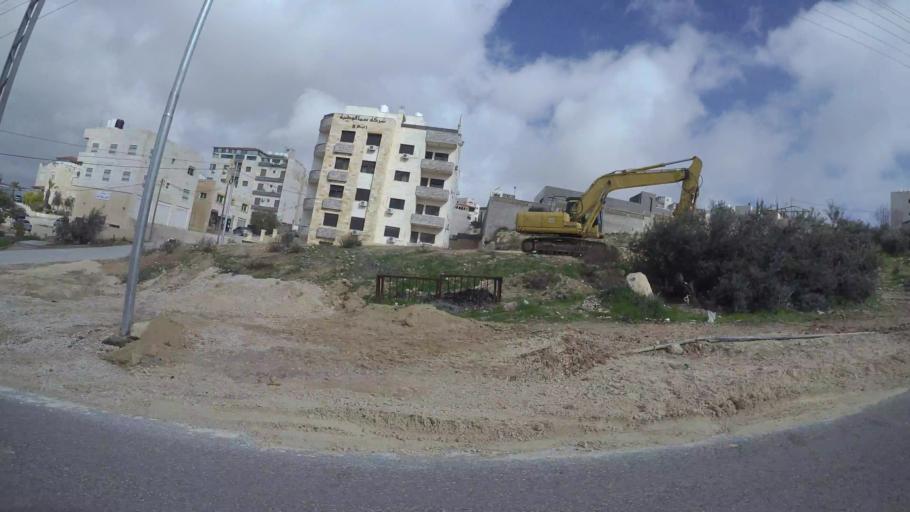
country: JO
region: Amman
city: Al Jubayhah
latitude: 32.0621
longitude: 35.8683
